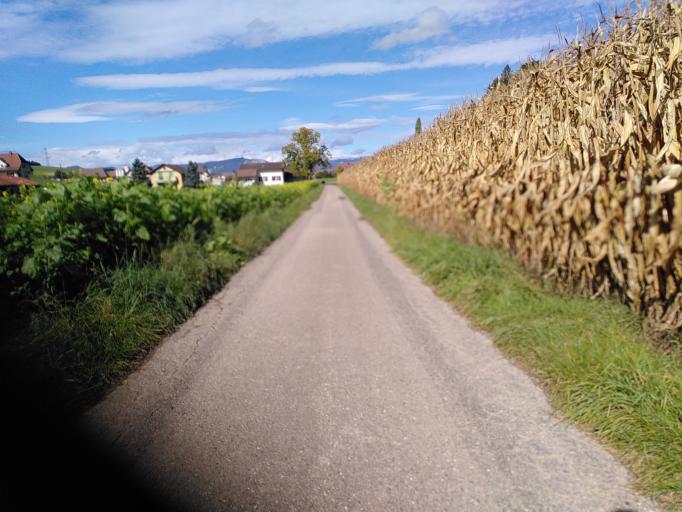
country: CH
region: Bern
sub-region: Oberaargau
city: Seeberg
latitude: 47.1375
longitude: 7.6739
